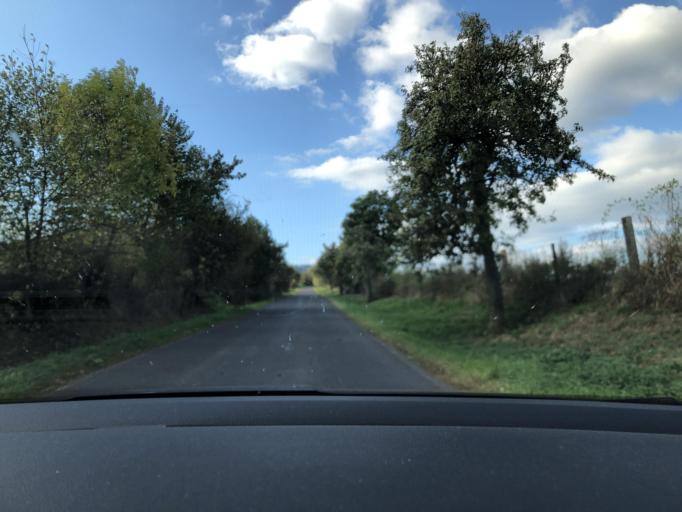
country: CZ
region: Ustecky
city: Zitenice
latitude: 50.5641
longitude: 14.1953
